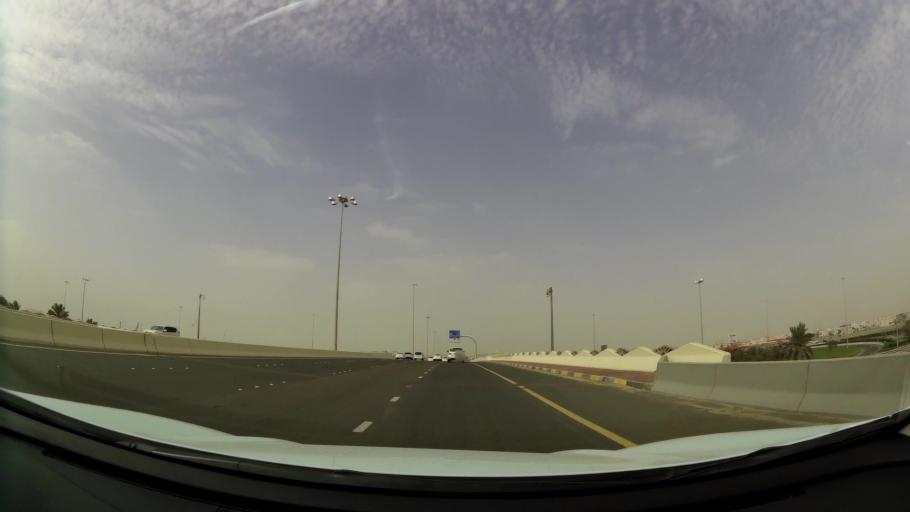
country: AE
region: Abu Dhabi
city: Abu Dhabi
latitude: 24.3973
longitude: 54.5744
